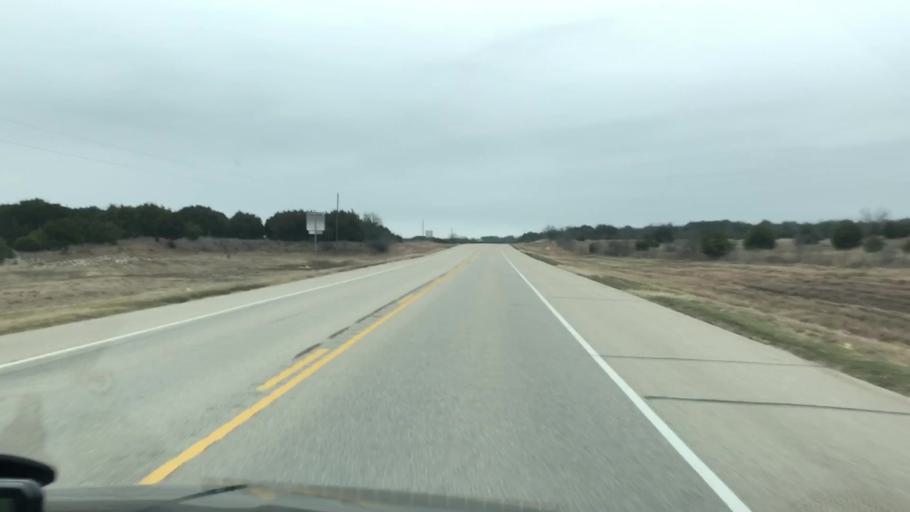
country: US
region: Texas
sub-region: Hamilton County
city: Hamilton
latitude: 31.8320
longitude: -98.1153
